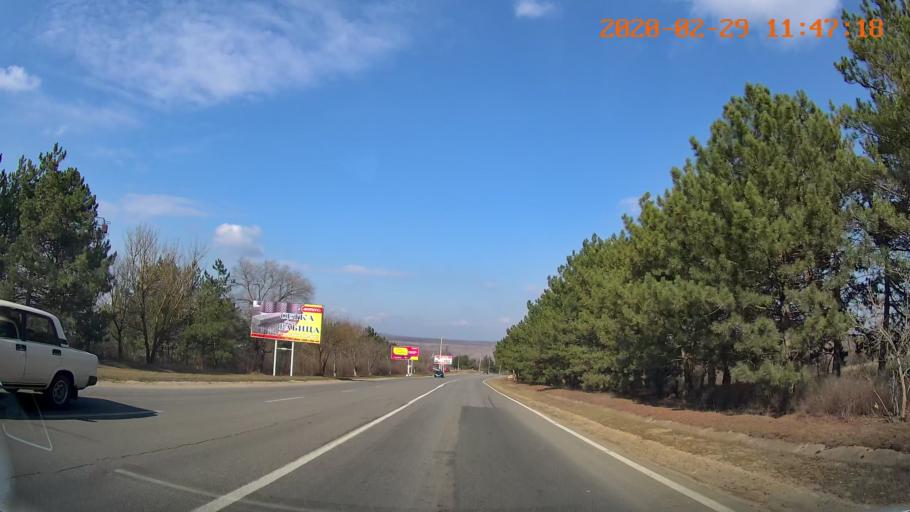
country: MD
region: Rezina
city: Rezina
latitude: 47.7392
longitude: 28.9889
